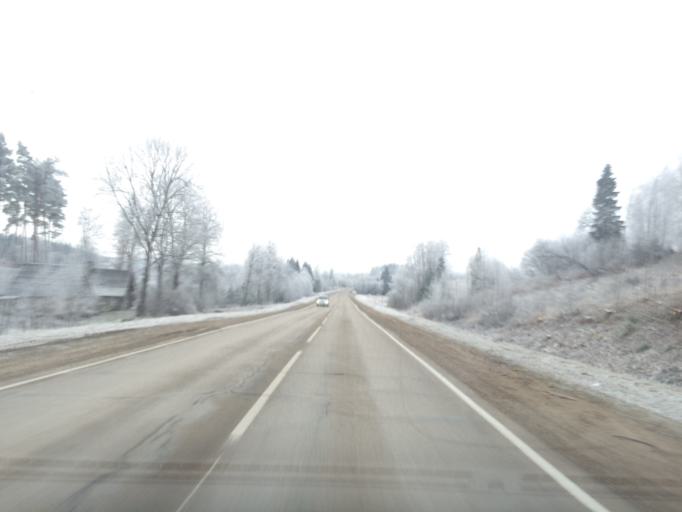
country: LV
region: Rezekne
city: Rezekne
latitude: 56.5944
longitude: 27.4156
